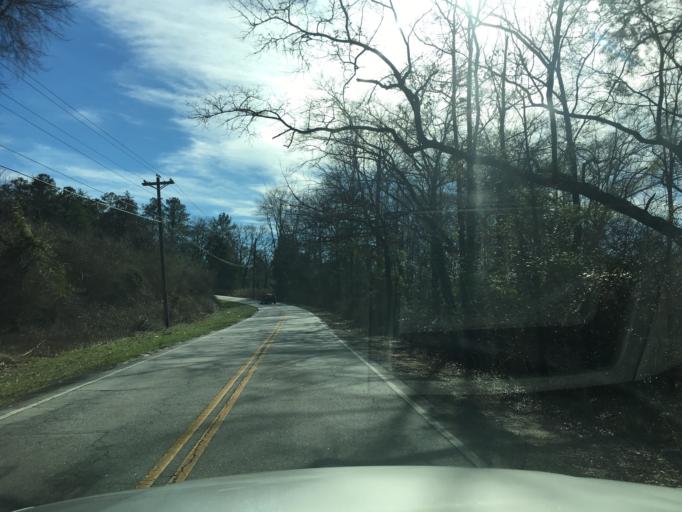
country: US
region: Georgia
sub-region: Rockdale County
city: Lakeview Estates
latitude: 33.7586
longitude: -84.0479
